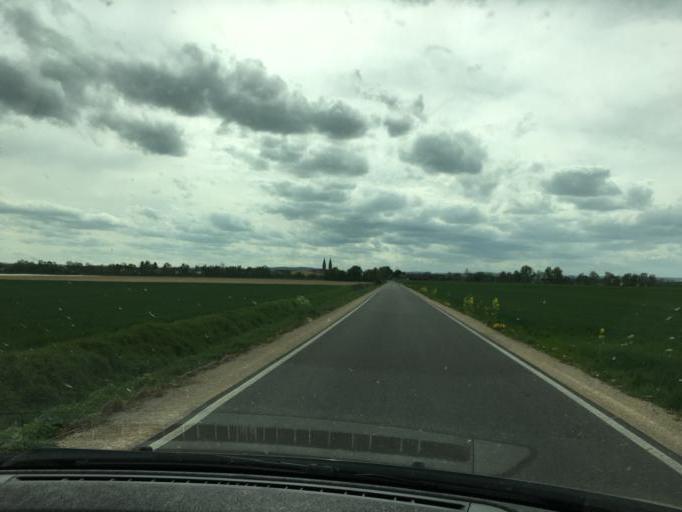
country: DE
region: North Rhine-Westphalia
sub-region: Regierungsbezirk Koln
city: Vettweiss
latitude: 50.7689
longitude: 6.5706
